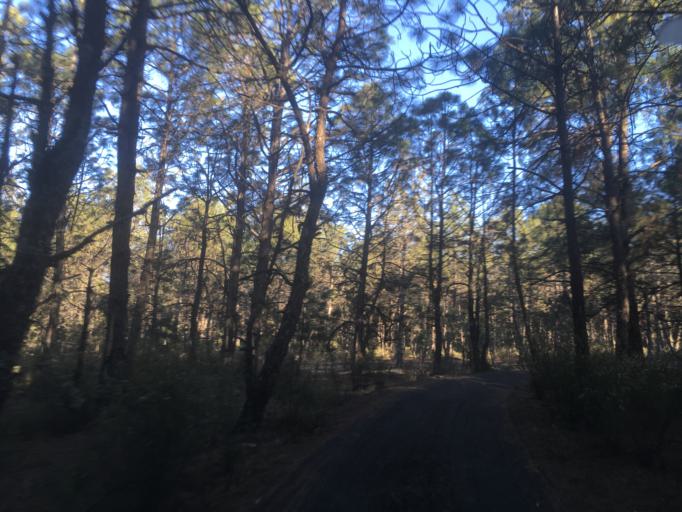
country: MX
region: Michoacan
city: Angahuan
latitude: 19.4635
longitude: -102.2390
